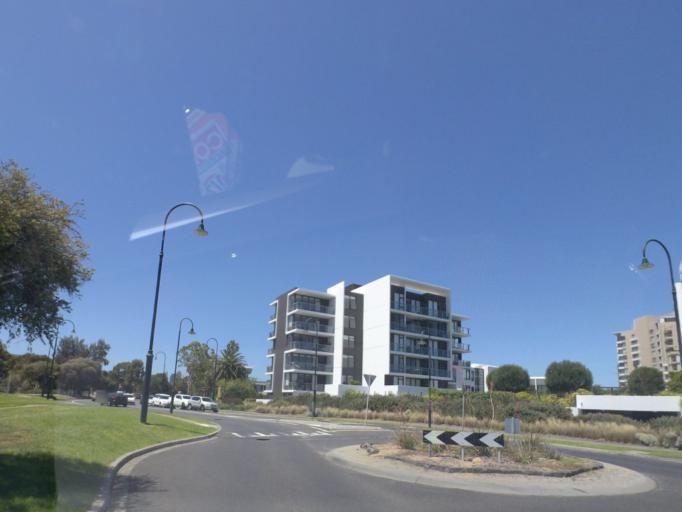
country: AU
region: Victoria
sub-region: Port Phillip
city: Port Melbourne
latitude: -37.8391
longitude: 144.9246
